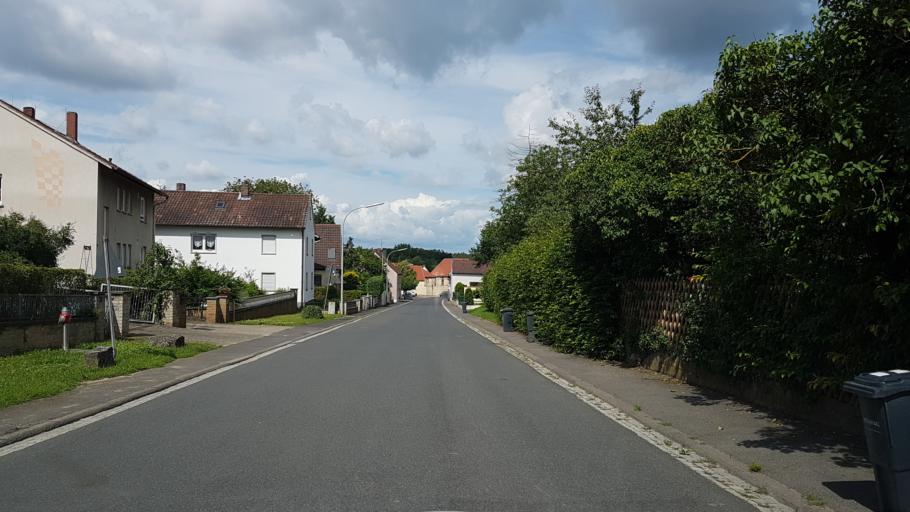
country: DE
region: Bavaria
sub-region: Regierungsbezirk Unterfranken
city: Kleinlangheim
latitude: 49.8123
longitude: 10.2933
